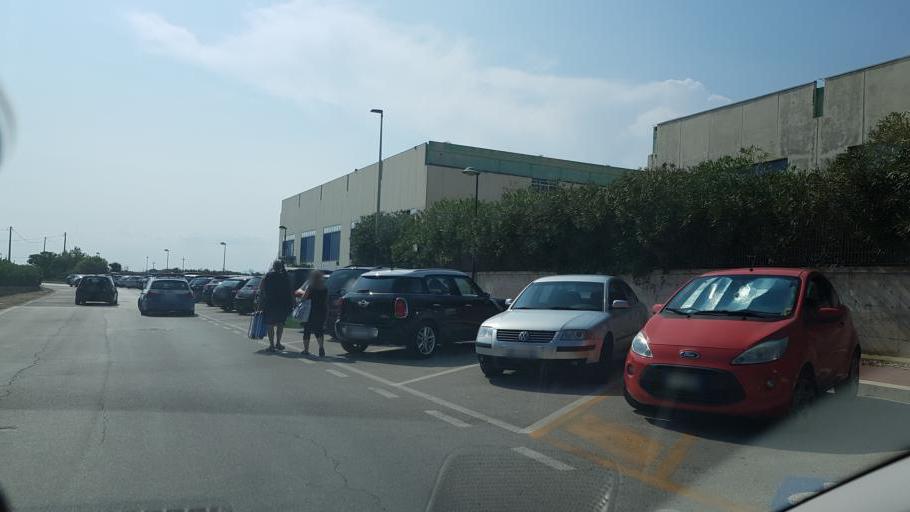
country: IT
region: Apulia
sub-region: Provincia di Bari
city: Monopoli
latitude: 40.9393
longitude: 17.3154
